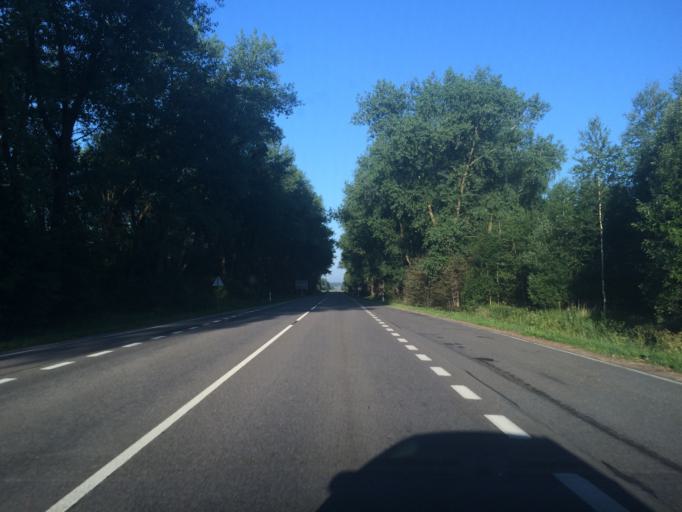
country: LT
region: Utenos apskritis
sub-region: Anyksciai
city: Anyksciai
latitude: 55.3933
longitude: 25.0730
